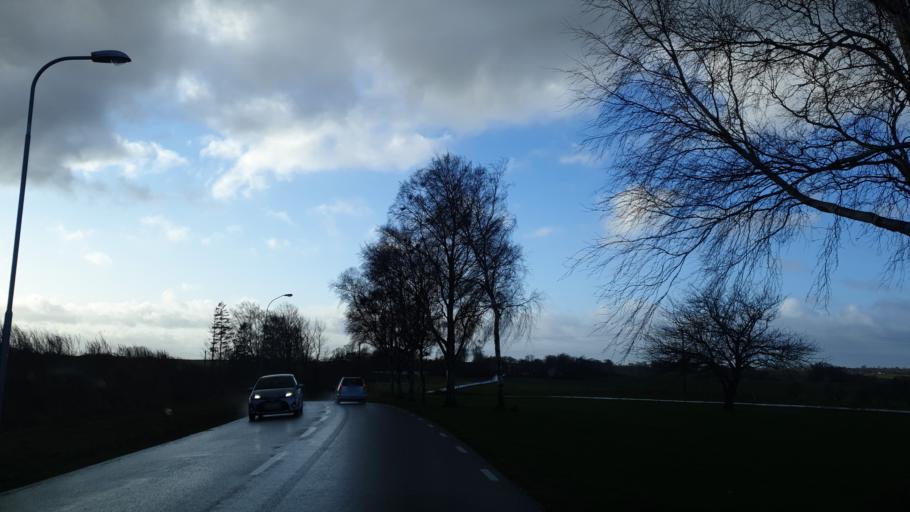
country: SE
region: Skane
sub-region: Skurups Kommun
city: Rydsgard
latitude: 55.4692
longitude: 13.5756
